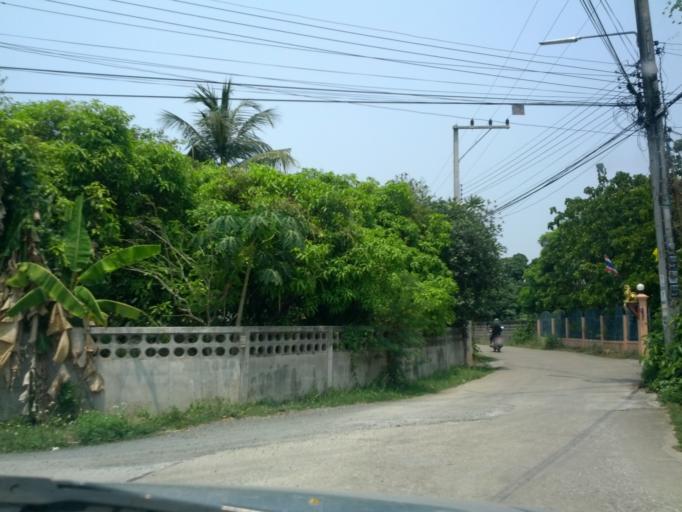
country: TH
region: Chiang Mai
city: San Sai
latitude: 18.8653
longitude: 99.0975
